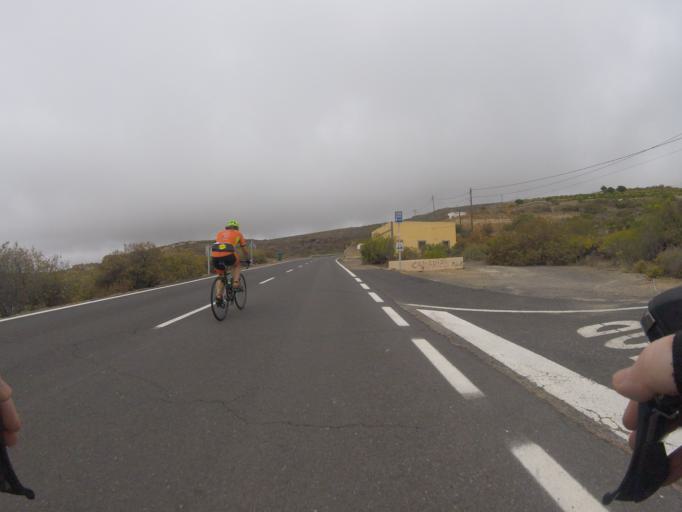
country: ES
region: Canary Islands
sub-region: Provincia de Santa Cruz de Tenerife
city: Fasnia
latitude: 28.2029
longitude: -16.4573
